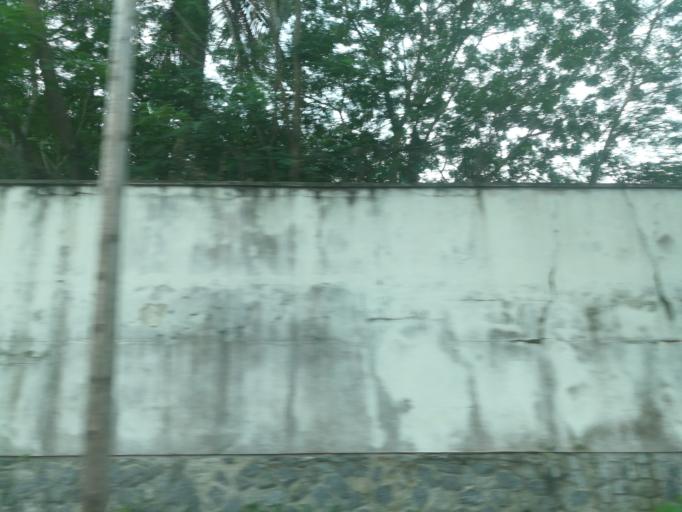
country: NG
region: Lagos
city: Lagos
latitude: 6.4375
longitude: 3.4105
